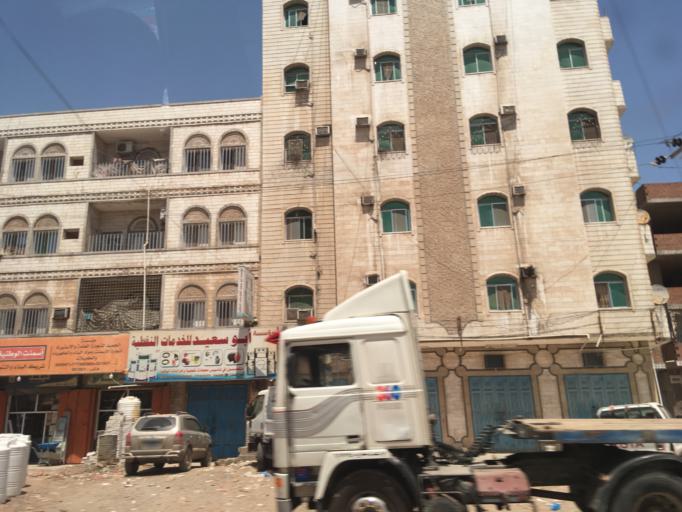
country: YE
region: Aden
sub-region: Al Mansura
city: Al Mansurah
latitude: 12.8621
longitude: 44.9720
